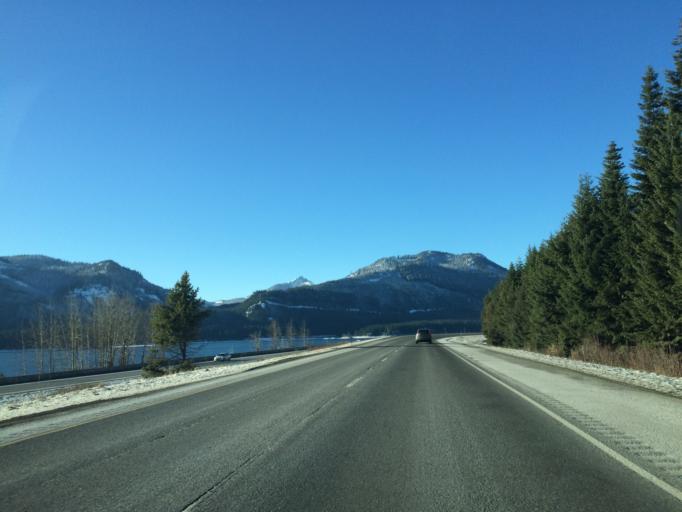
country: US
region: Washington
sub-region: Kittitas County
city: Cle Elum
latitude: 47.3297
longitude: -121.3405
